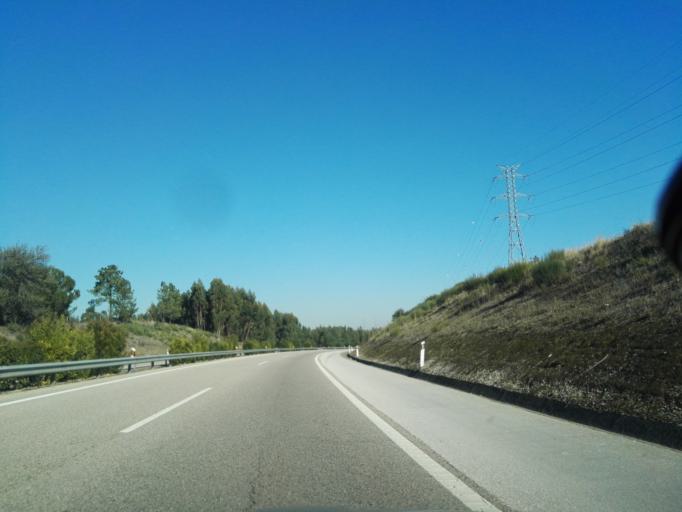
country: PT
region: Santarem
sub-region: Entroncamento
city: Entroncamento
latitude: 39.4835
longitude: -8.4761
